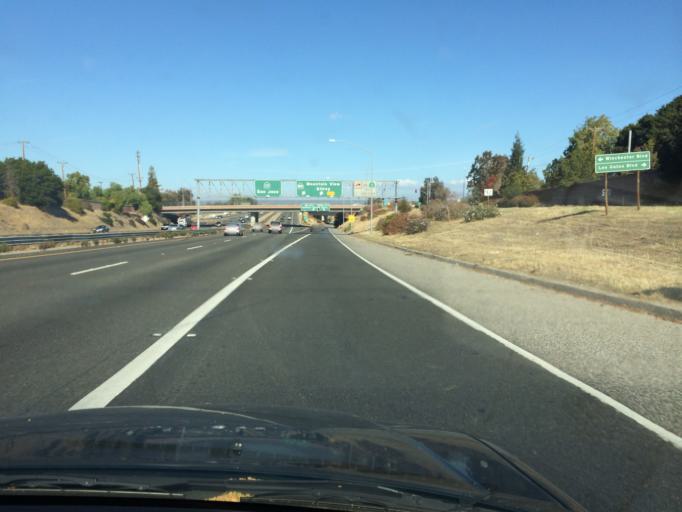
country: US
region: California
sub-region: Santa Clara County
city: Los Gatos
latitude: 37.2475
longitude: -121.9604
